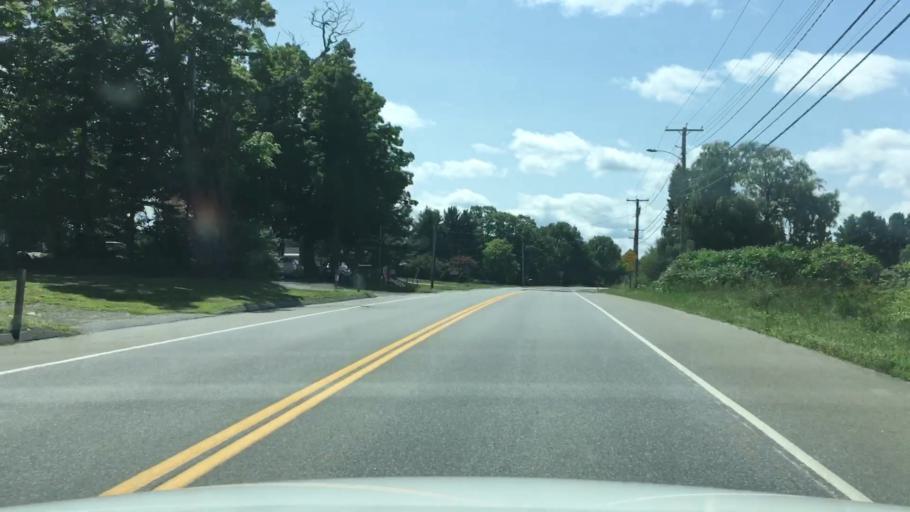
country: US
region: Maine
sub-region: Kennebec County
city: Augusta
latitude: 44.2951
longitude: -69.7684
